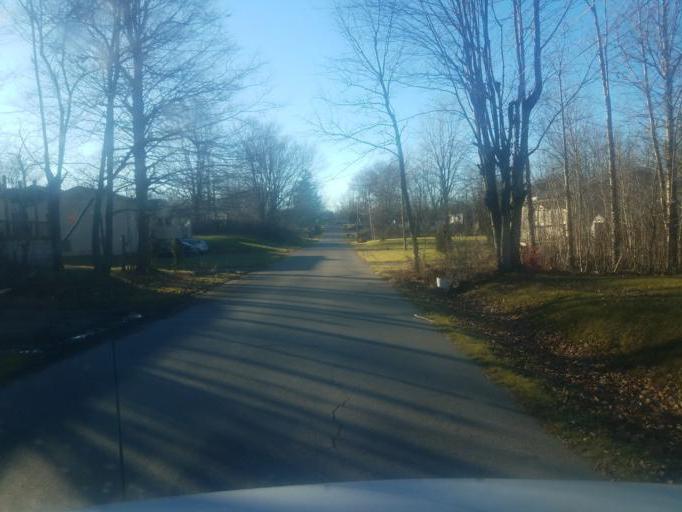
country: US
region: Ohio
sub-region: Richland County
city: Mansfield
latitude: 40.7885
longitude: -82.5358
